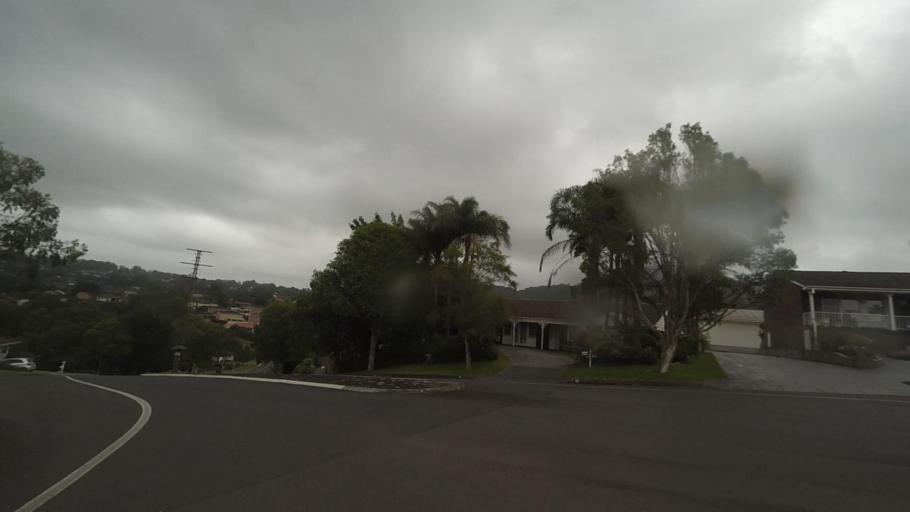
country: AU
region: New South Wales
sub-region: Wollongong
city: Cordeaux Heights
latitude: -34.4506
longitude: 150.8310
